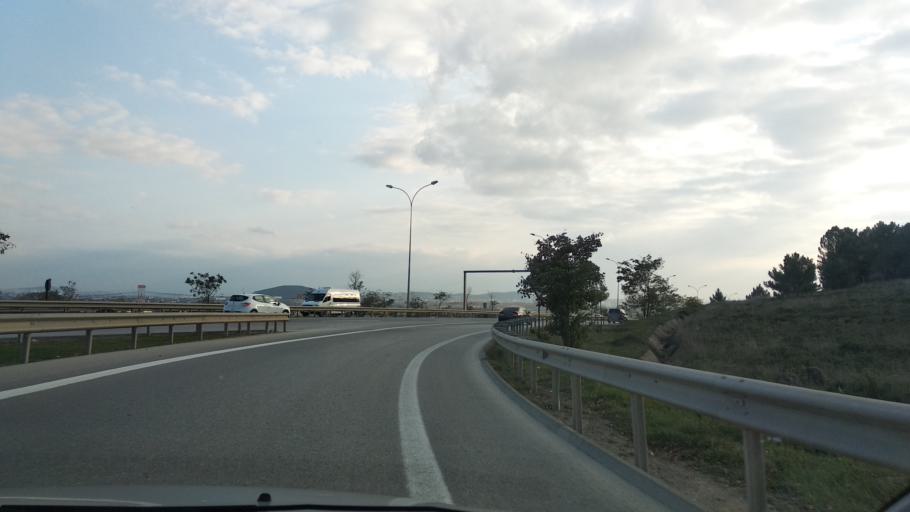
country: TR
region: Istanbul
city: Sultanbeyli
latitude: 40.9207
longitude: 29.3393
